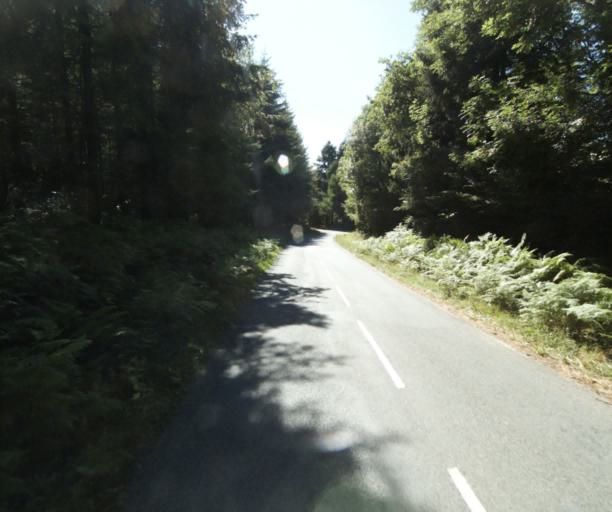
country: FR
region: Midi-Pyrenees
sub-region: Departement du Tarn
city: Soreze
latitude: 43.4319
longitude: 2.1170
